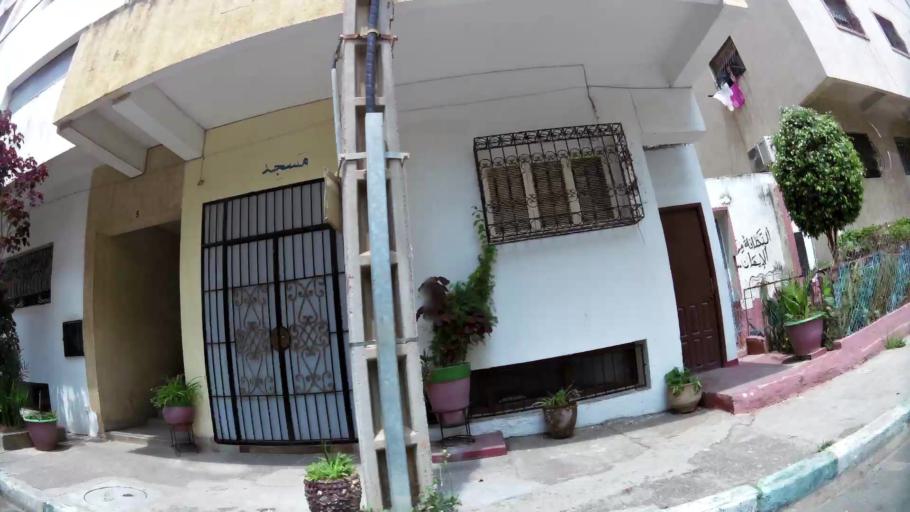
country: MA
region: Rabat-Sale-Zemmour-Zaer
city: Sale
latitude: 34.0508
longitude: -6.8147
